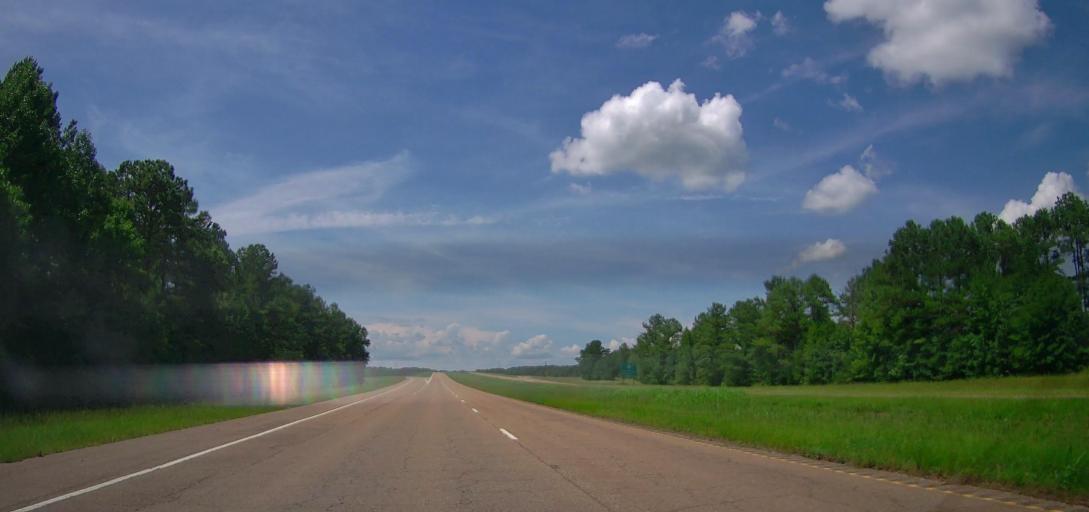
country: US
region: Mississippi
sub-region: Monroe County
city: Aberdeen
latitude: 33.8339
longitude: -88.5888
